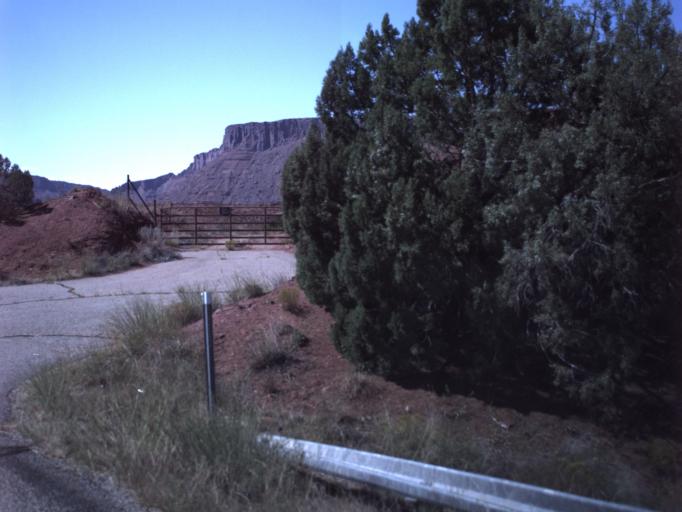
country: US
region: Utah
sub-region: Grand County
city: Moab
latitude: 38.7280
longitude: -109.3499
